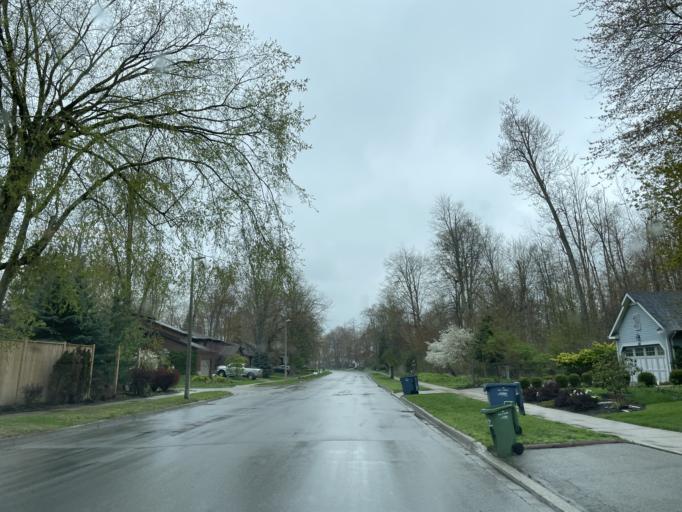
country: CA
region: Ontario
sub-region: Wellington County
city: Guelph
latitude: 43.5345
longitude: -80.2912
